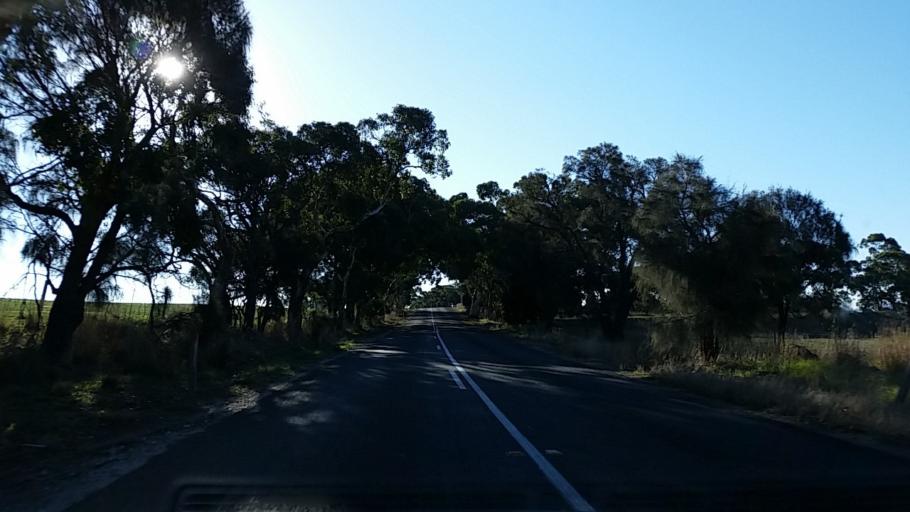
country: AU
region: South Australia
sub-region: Mount Barker
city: Mount Barker
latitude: -35.1373
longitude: 138.9173
